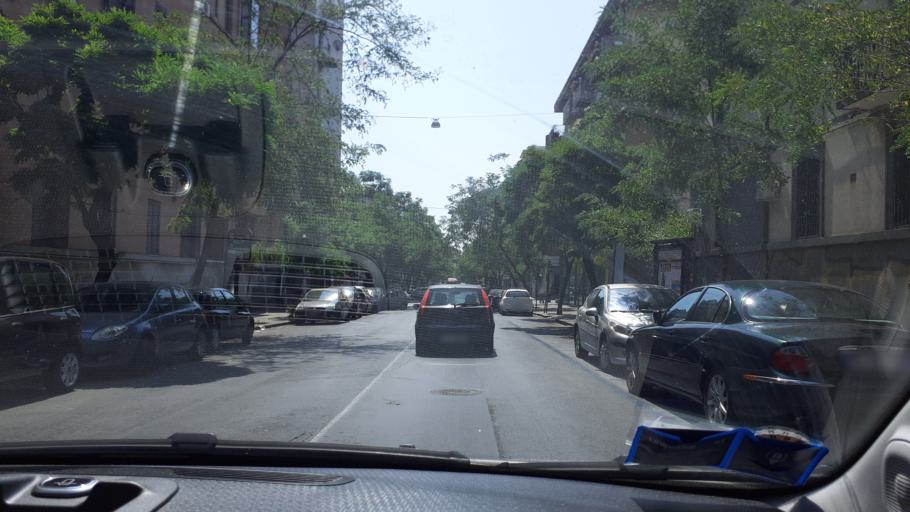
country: IT
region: Sicily
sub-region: Catania
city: Catania
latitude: 37.5125
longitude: 15.0746
